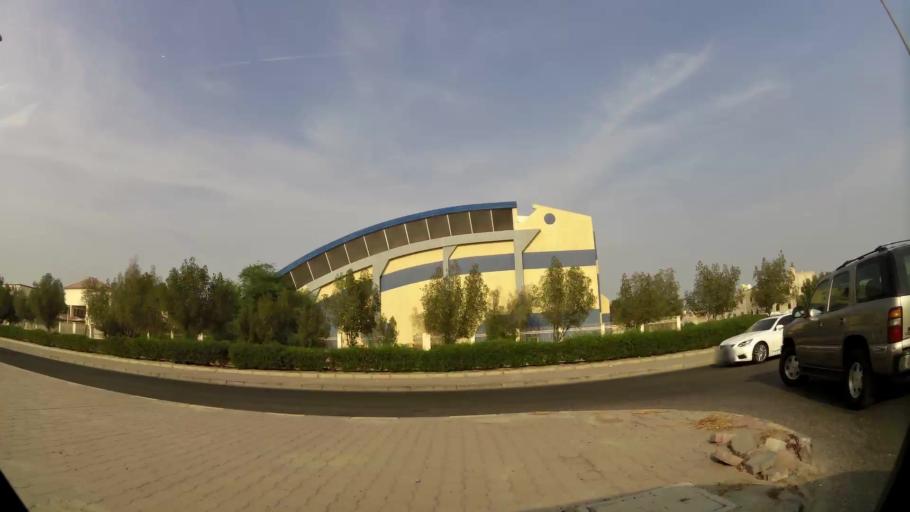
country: KW
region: Mubarak al Kabir
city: Sabah as Salim
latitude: 29.2464
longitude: 48.0560
